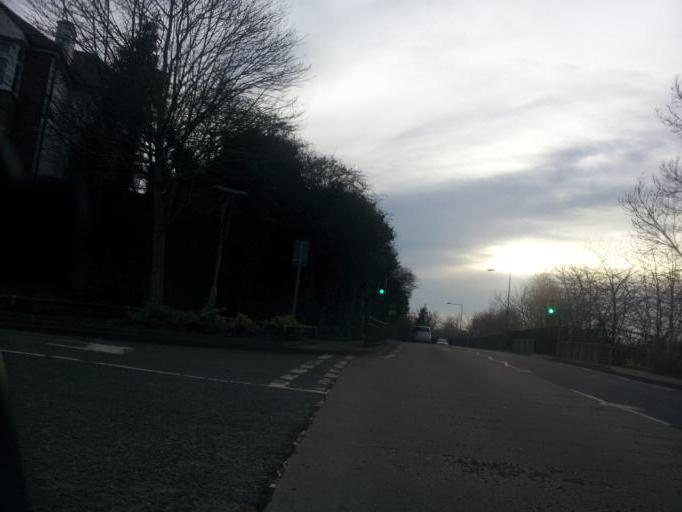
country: GB
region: England
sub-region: Kent
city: Gravesend
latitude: 51.4287
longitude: 0.3644
